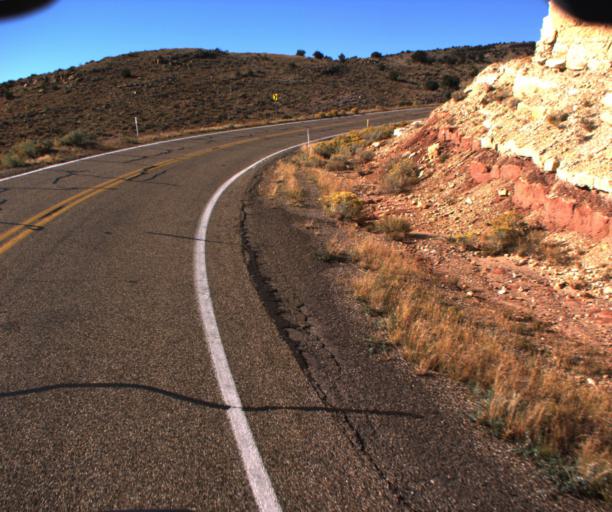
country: US
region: Arizona
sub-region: Coconino County
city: Fredonia
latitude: 36.7319
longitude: -112.0590
